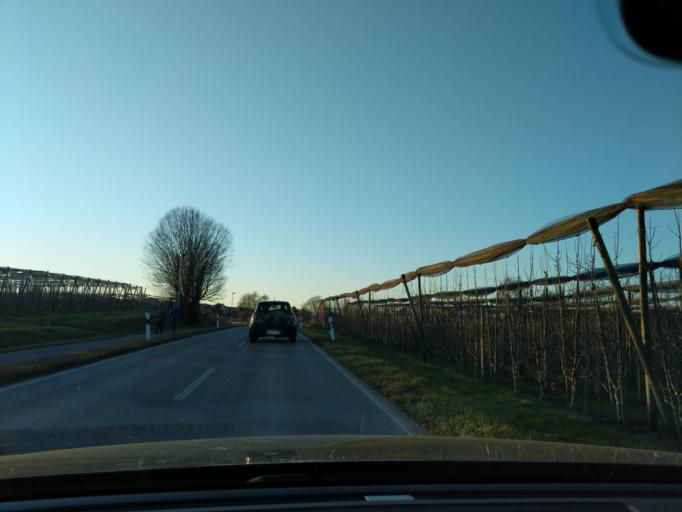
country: DE
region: Baden-Wuerttemberg
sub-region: Tuebingen Region
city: Immenstaad am Bodensee
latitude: 47.6705
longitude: 9.3592
